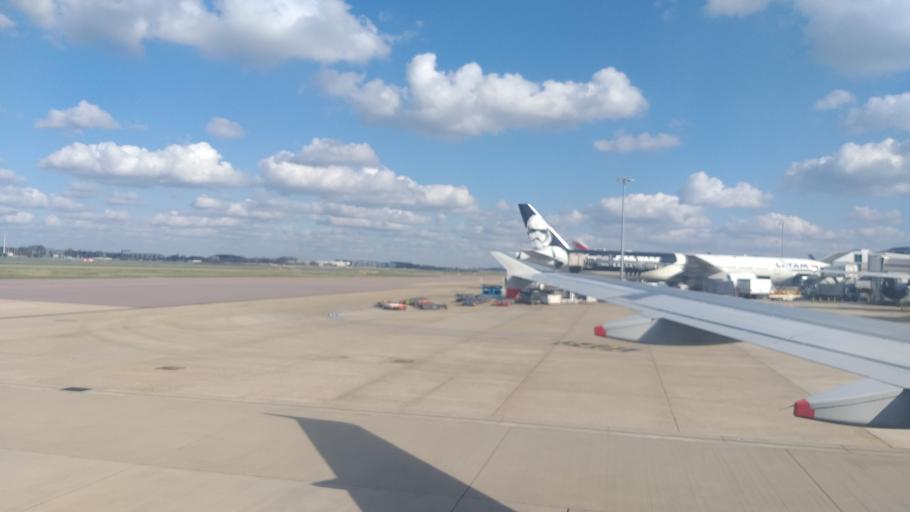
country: GB
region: England
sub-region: Greater London
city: West Drayton
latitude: 51.4745
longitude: -0.4674
